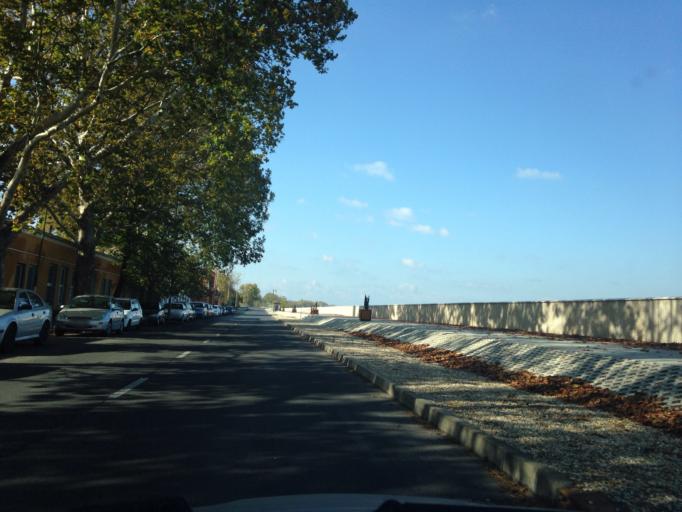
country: HU
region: Komarom-Esztergom
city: Komarom
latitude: 47.7497
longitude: 18.1161
